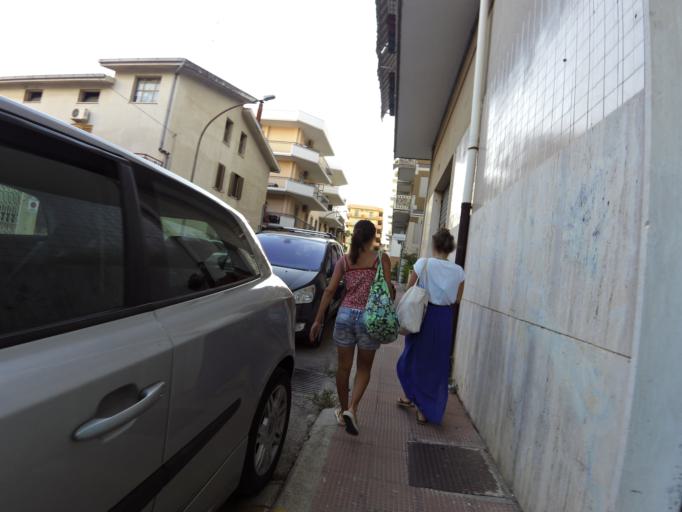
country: IT
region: Calabria
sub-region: Provincia di Catanzaro
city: Soverato Marina
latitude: 38.6881
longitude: 16.5532
